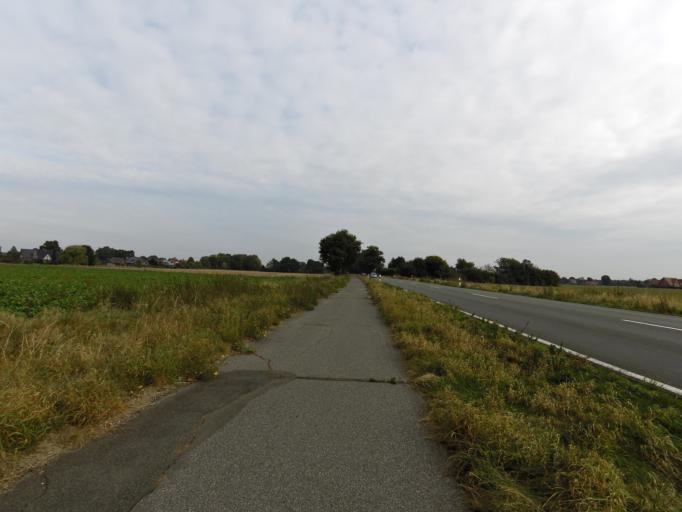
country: DE
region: North Rhine-Westphalia
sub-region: Regierungsbezirk Dusseldorf
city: Bocholt
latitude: 51.8302
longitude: 6.5412
